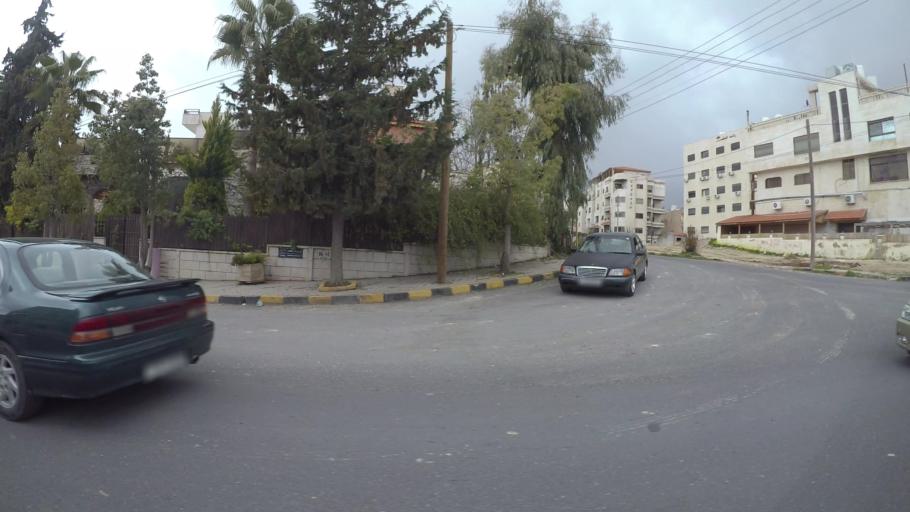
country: JO
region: Amman
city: Wadi as Sir
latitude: 31.9710
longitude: 35.8522
